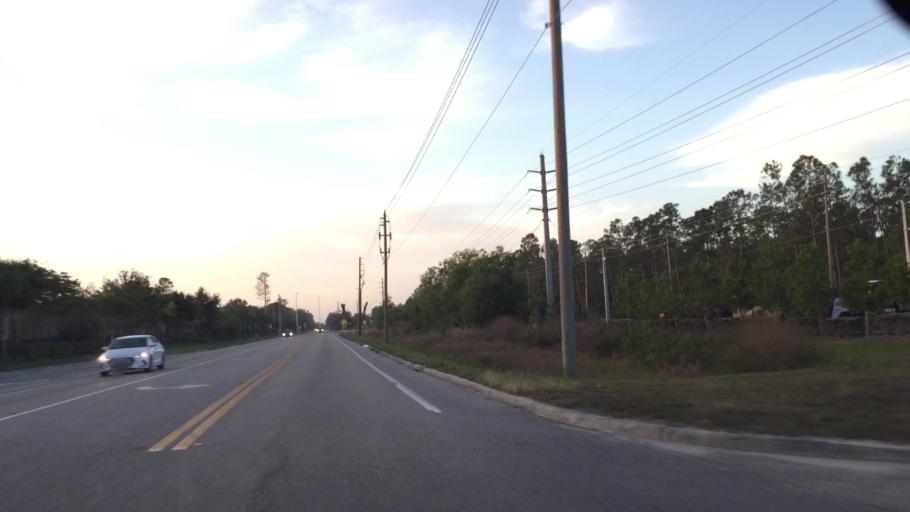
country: US
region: Florida
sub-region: Lee County
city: Villas
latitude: 26.5674
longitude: -81.8471
